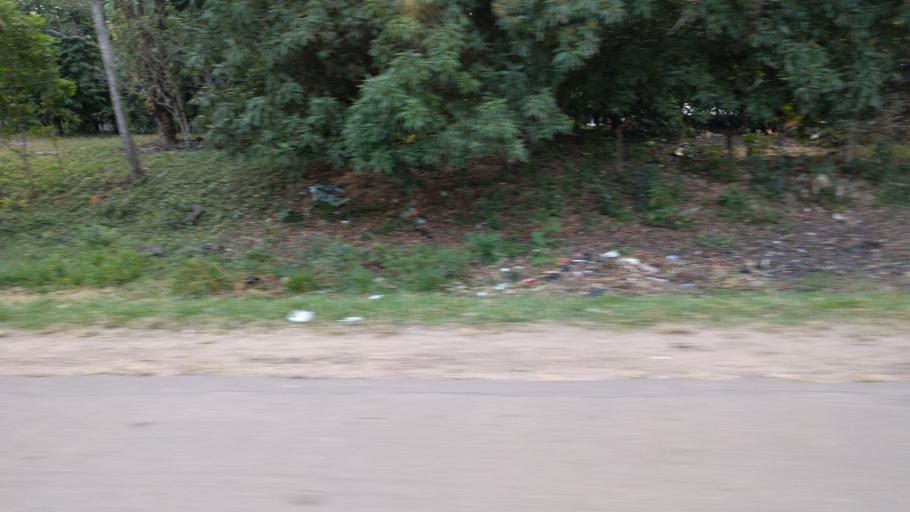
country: BO
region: Santa Cruz
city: Buena Vista
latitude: -17.4123
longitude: -63.6149
